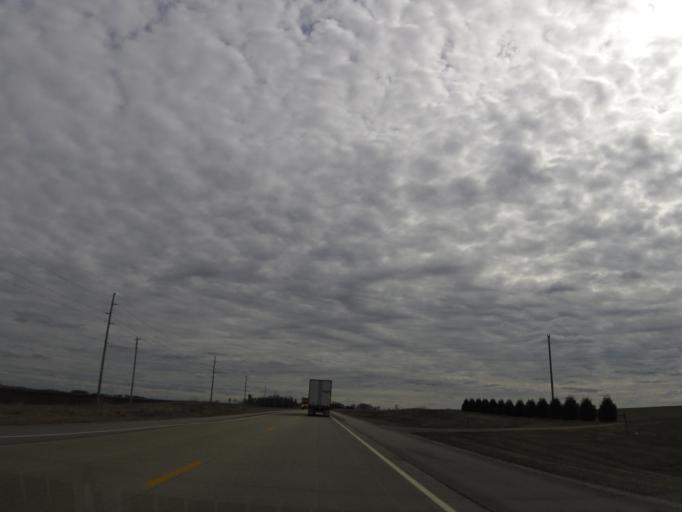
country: US
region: Minnesota
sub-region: Fillmore County
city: Spring Valley
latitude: 43.5865
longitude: -92.3893
